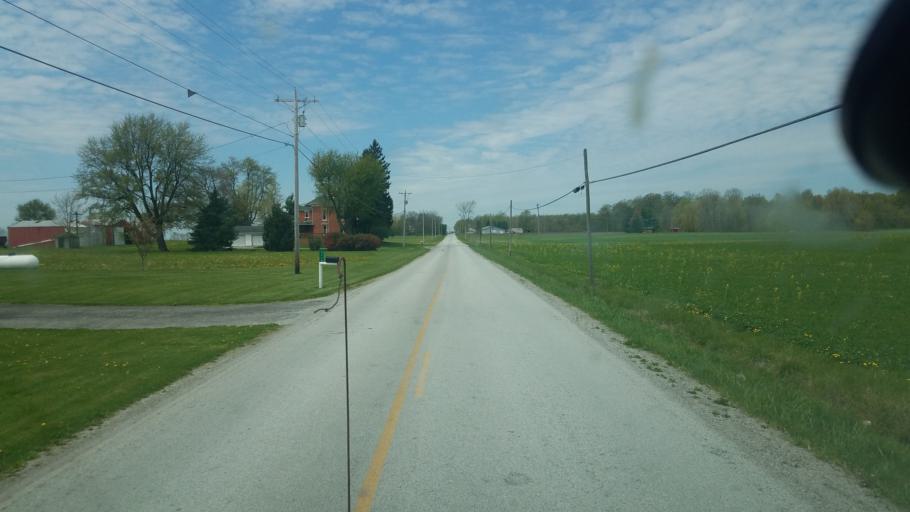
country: US
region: Ohio
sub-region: Hardin County
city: Ada
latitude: 40.7094
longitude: -83.7975
